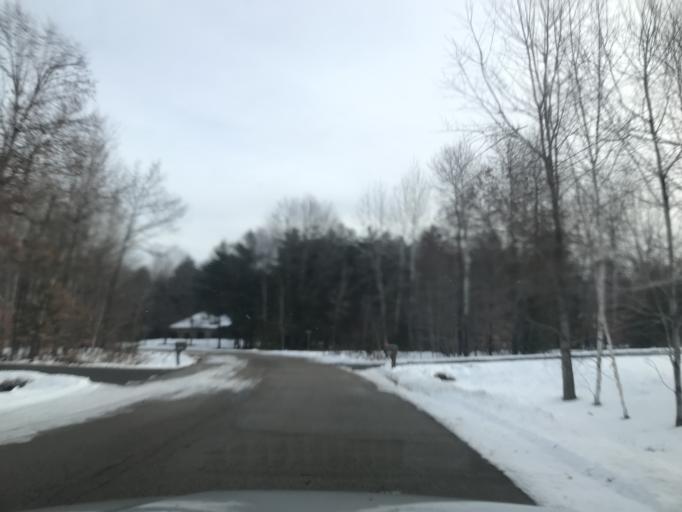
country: US
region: Wisconsin
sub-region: Brown County
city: Suamico
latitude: 44.6896
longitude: -88.0625
